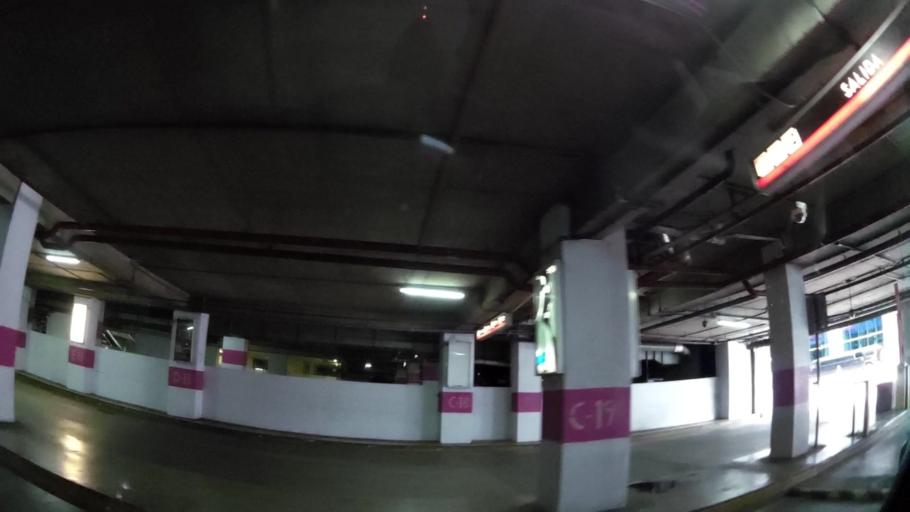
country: PA
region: Panama
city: Panama
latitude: 8.9764
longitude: -79.5175
